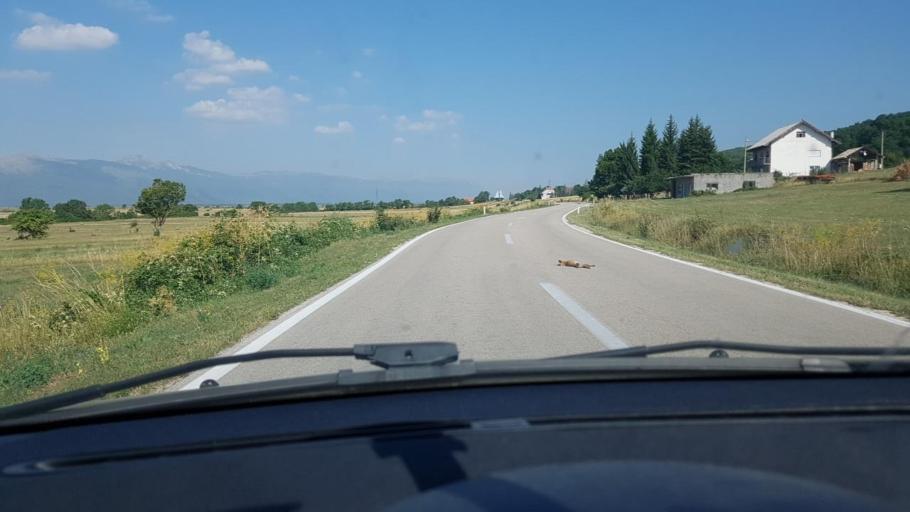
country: BA
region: Federation of Bosnia and Herzegovina
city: Orguz
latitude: 43.8971
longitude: 16.8174
